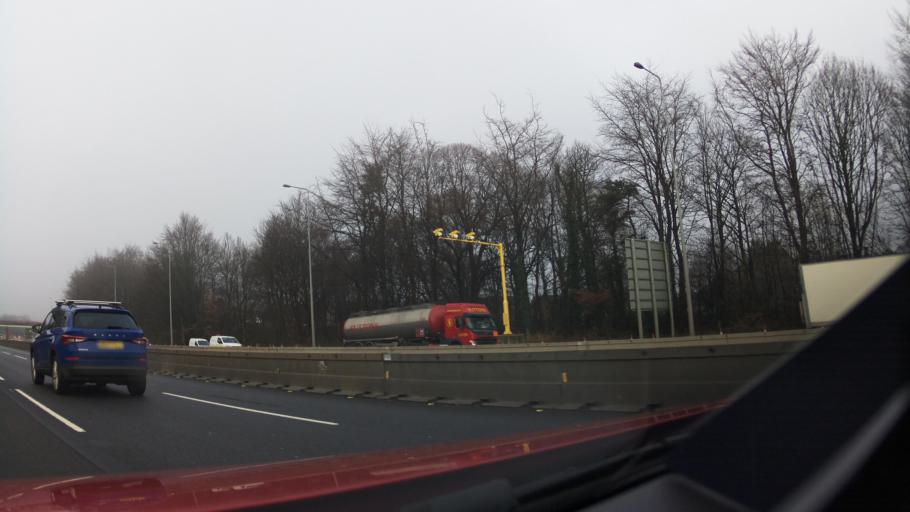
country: GB
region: England
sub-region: Borough of Wigan
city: Ashton in Makerfield
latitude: 53.4843
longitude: -2.6505
